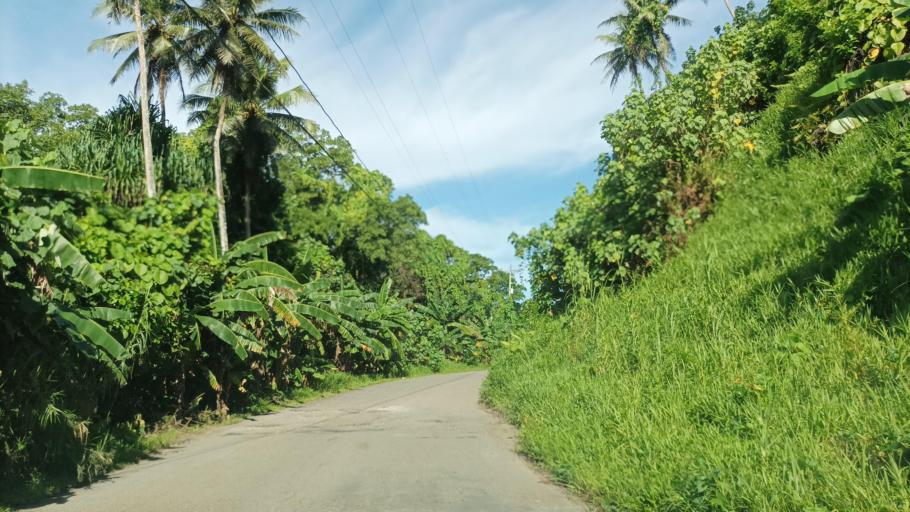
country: FM
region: Kosrae
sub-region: Lelu Municipality
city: Tofol
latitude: 5.3211
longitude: 163.0142
